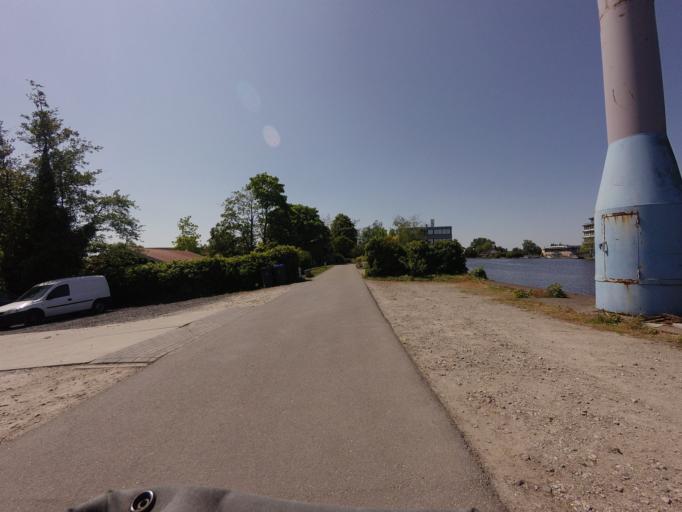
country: NL
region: North Holland
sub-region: Gemeente Uithoorn
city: Uithoorn
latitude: 52.2374
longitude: 4.8464
